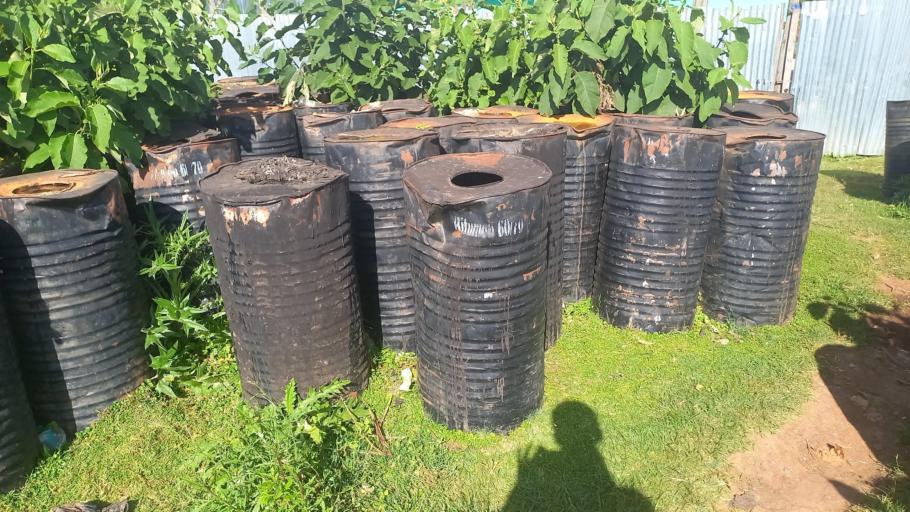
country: ET
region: Southern Nations, Nationalities, and People's Region
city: K'olito
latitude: 7.5505
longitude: 37.8637
